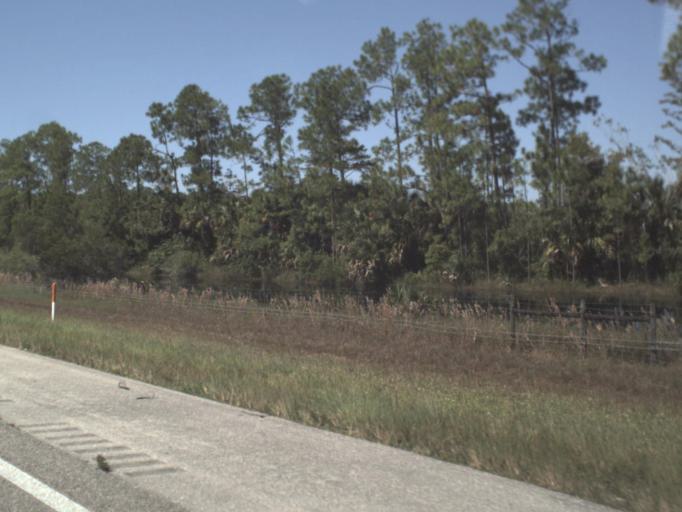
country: US
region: Florida
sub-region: Collier County
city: Golden Gate
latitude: 26.1548
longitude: -81.6340
